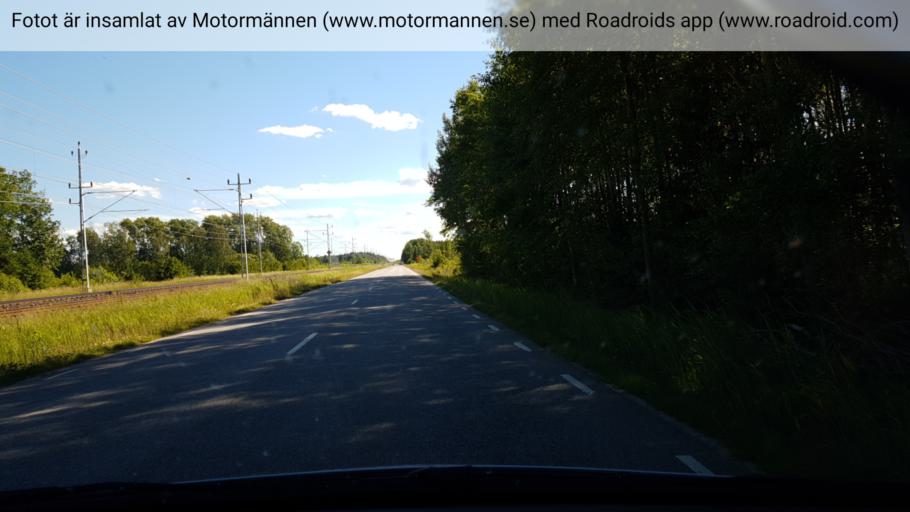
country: SE
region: Vaestra Goetaland
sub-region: Toreboda Kommun
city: Toereboda
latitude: 58.6834
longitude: 14.1076
